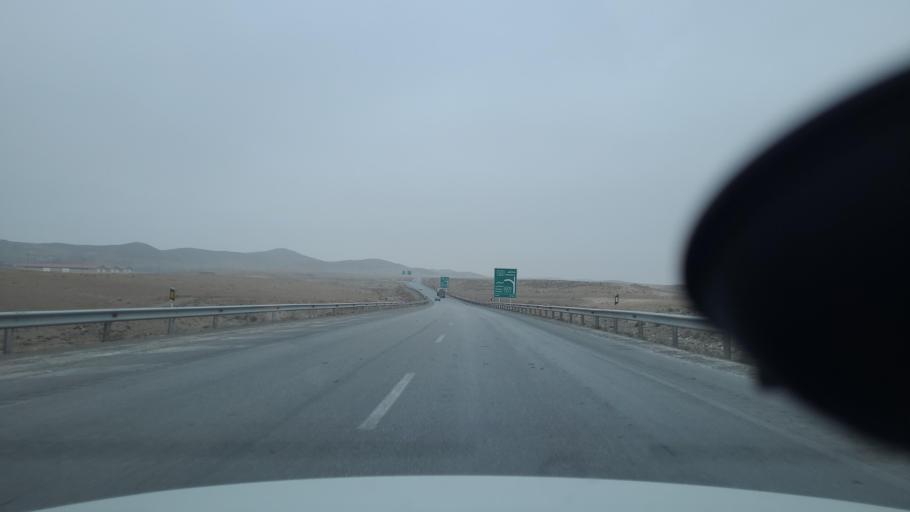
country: IR
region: Razavi Khorasan
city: Fariman
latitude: 35.9934
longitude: 59.7512
